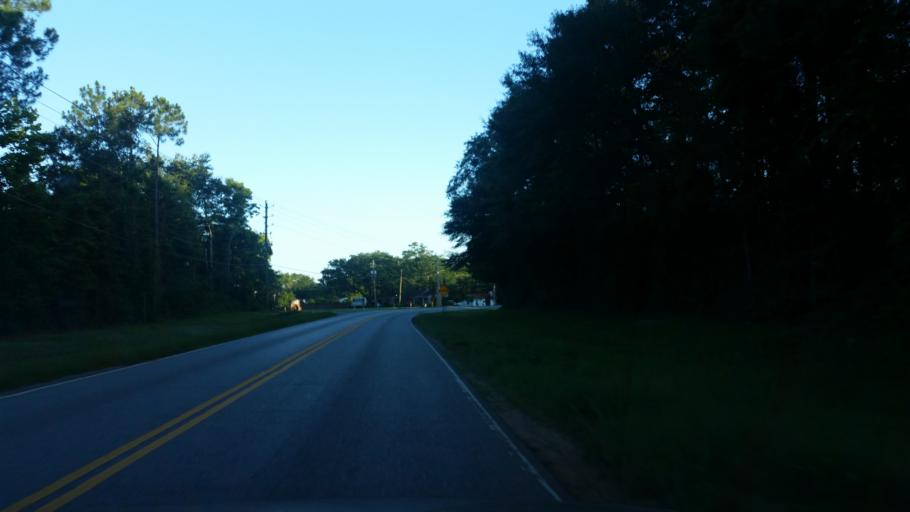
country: US
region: Florida
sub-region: Escambia County
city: Cantonment
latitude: 30.6025
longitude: -87.3305
